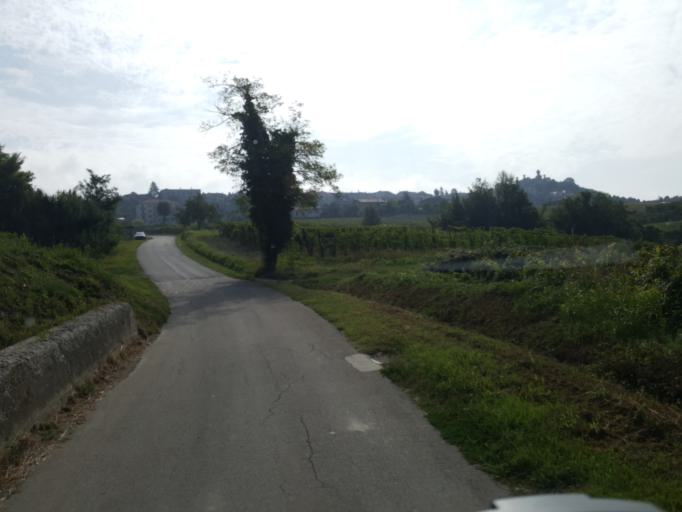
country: IT
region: Piedmont
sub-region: Provincia di Cuneo
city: Novello
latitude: 44.5904
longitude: 7.9203
